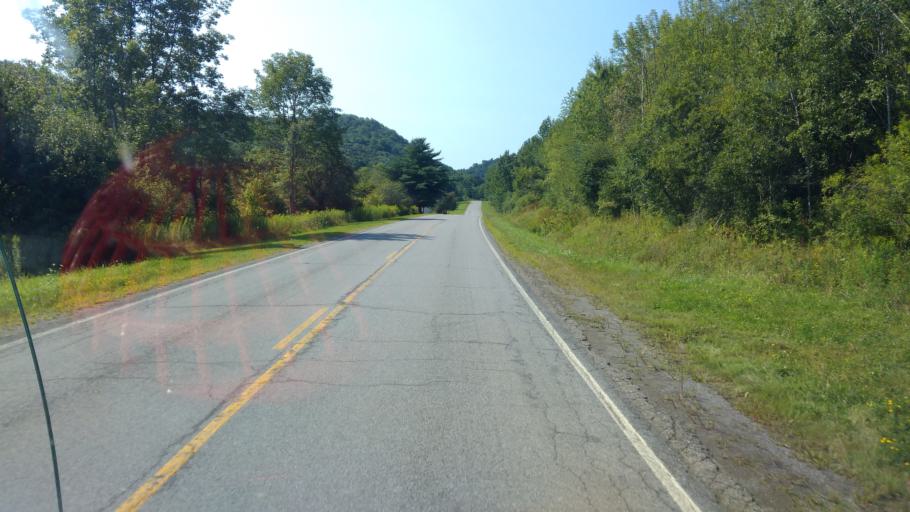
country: US
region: New York
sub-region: Allegany County
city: Bolivar
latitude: 42.1279
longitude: -78.1545
